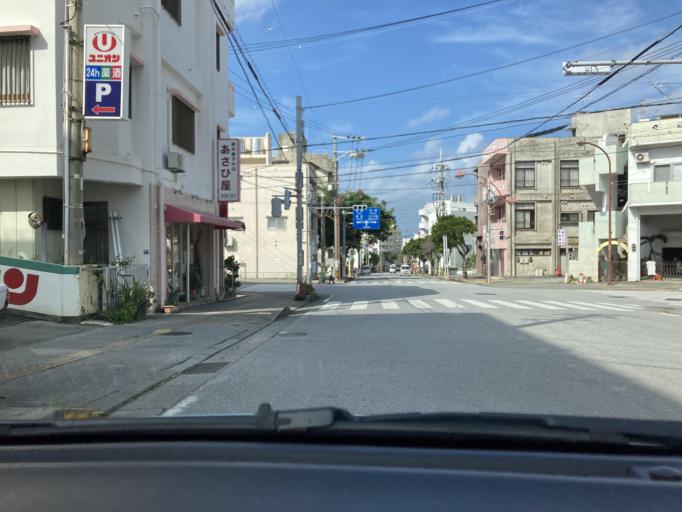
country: JP
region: Okinawa
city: Chatan
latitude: 26.2895
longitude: 127.7810
